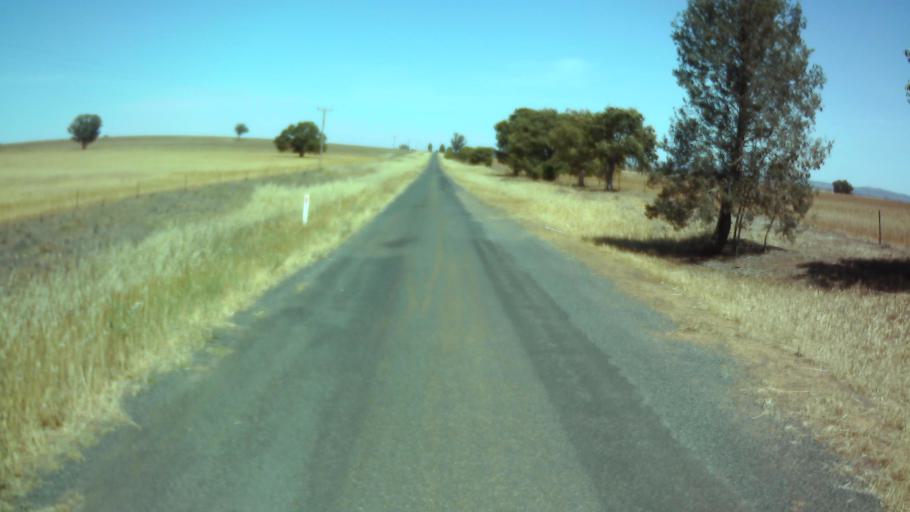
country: AU
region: New South Wales
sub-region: Weddin
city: Grenfell
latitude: -33.8638
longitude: 147.9941
